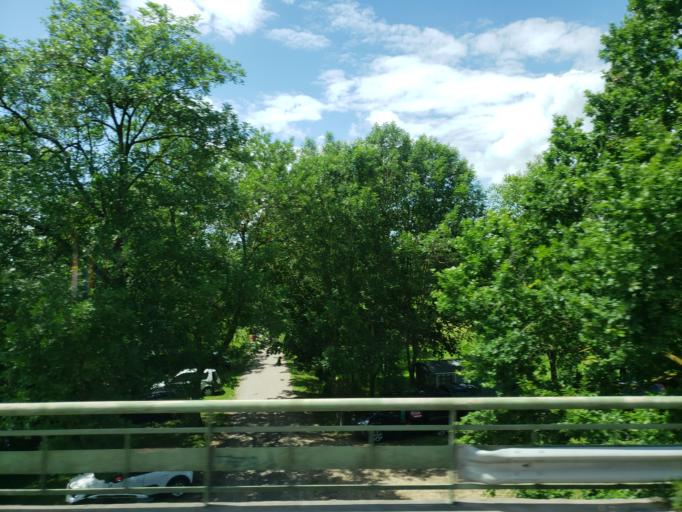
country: FR
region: Bourgogne
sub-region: Departement de l'Yonne
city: Migennes
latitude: 47.9551
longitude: 3.5048
